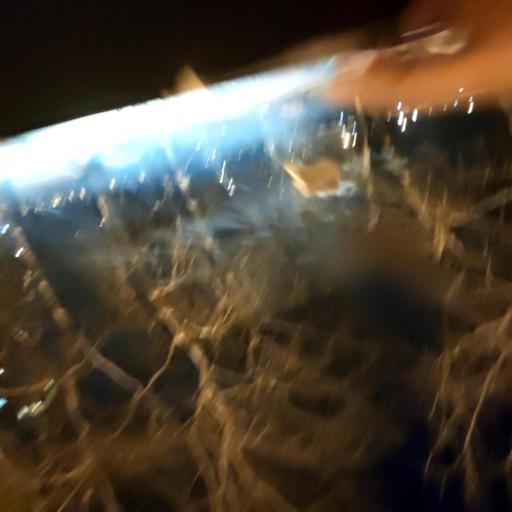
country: RU
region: Perm
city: Perm
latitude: 58.0148
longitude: 56.2182
